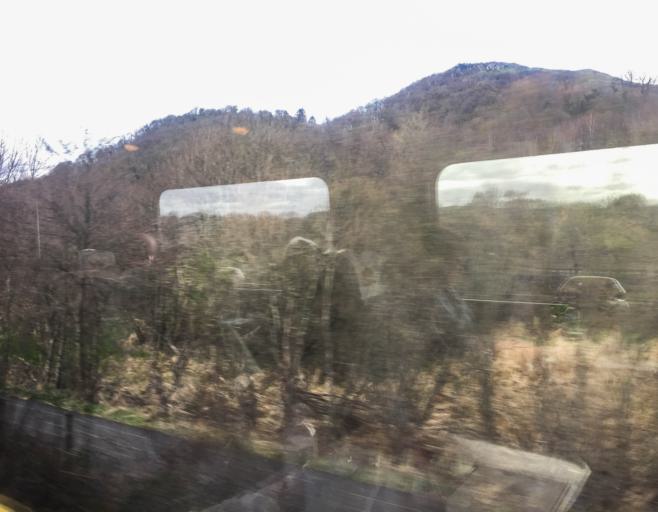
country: GB
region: Scotland
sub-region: Renfrewshire
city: Bishopton
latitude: 55.9331
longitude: -4.5100
